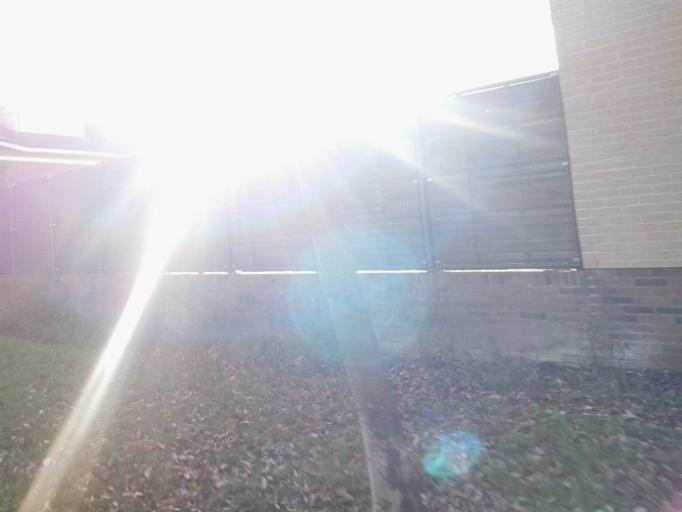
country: NL
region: South Holland
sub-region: Gemeente Lansingerland
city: Bergschenhoek
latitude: 51.9856
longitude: 4.4922
